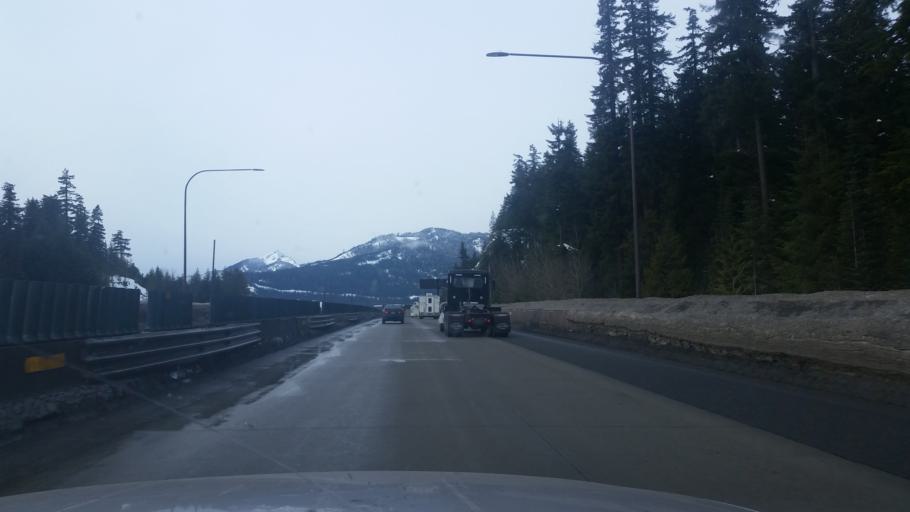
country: US
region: Washington
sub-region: Kittitas County
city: Cle Elum
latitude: 47.3274
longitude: -121.3333
